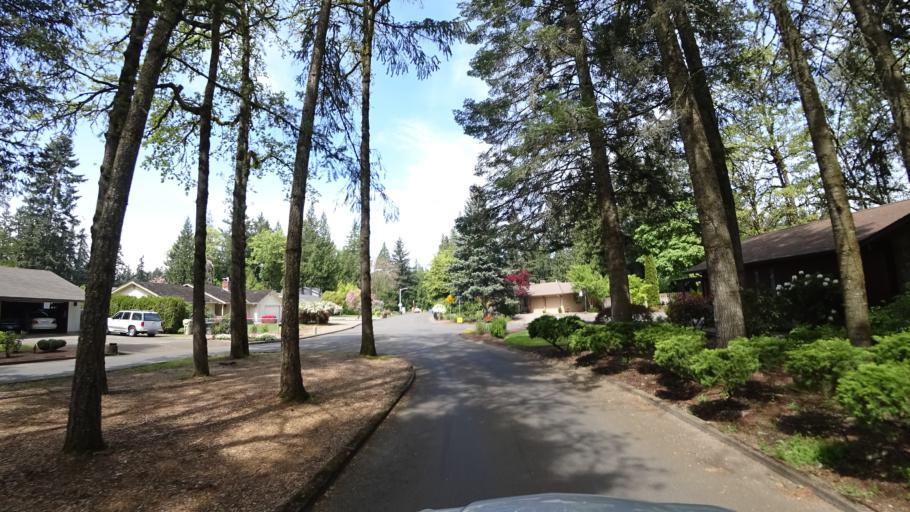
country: US
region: Oregon
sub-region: Washington County
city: Rockcreek
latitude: 45.5150
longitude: -122.9217
